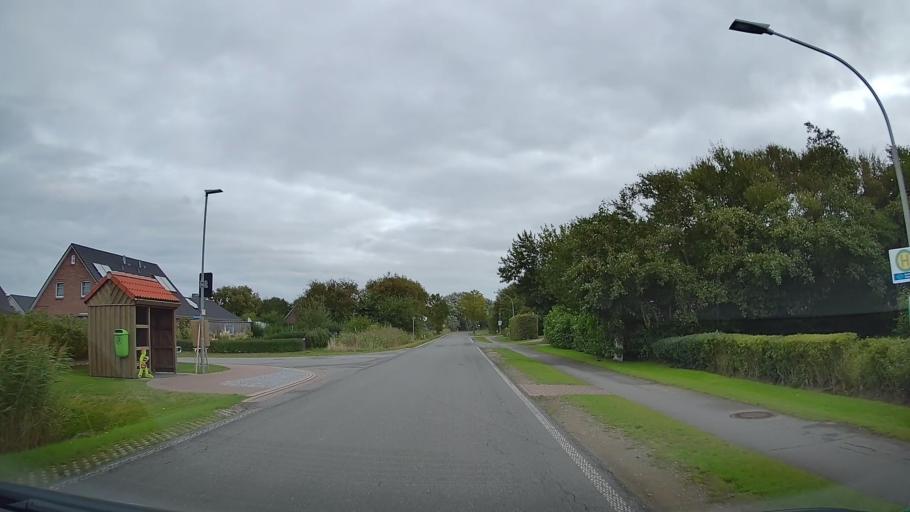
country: DE
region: Schleswig-Holstein
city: Klanxbull
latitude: 54.8669
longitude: 8.6725
